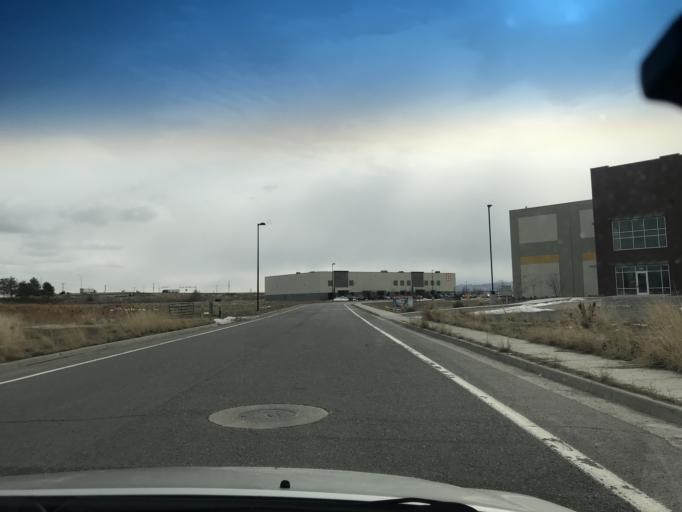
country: US
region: Utah
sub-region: Salt Lake County
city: West Valley City
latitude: 40.7748
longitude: -112.0272
